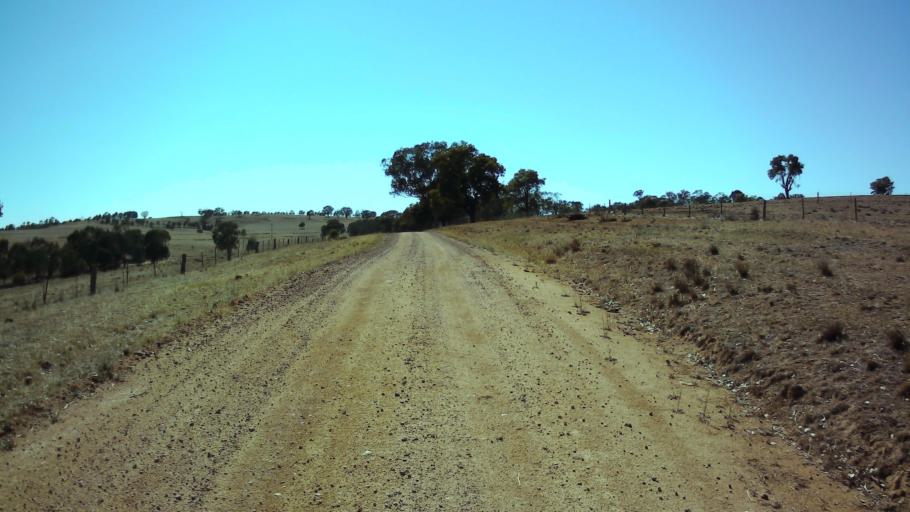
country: AU
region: New South Wales
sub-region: Cowra
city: Cowra
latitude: -33.9697
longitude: 148.4549
